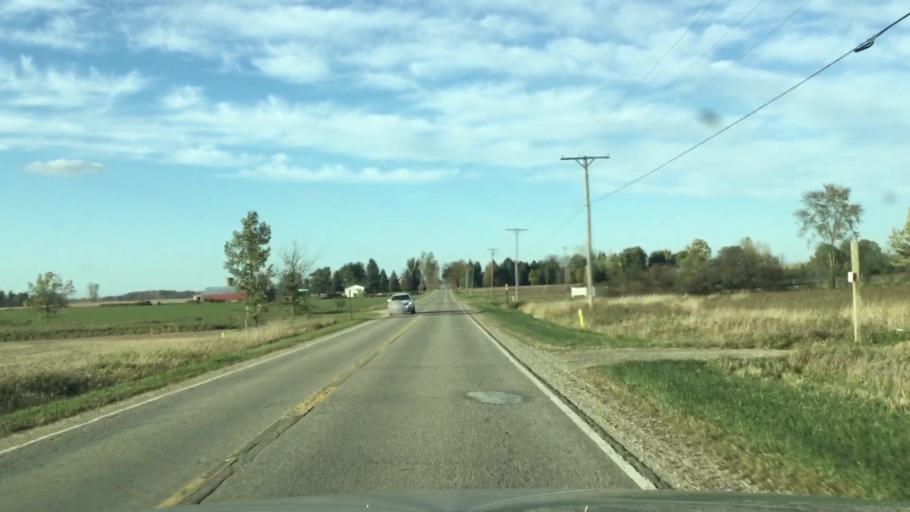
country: US
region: Michigan
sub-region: Lapeer County
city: North Branch
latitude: 43.2954
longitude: -83.1987
